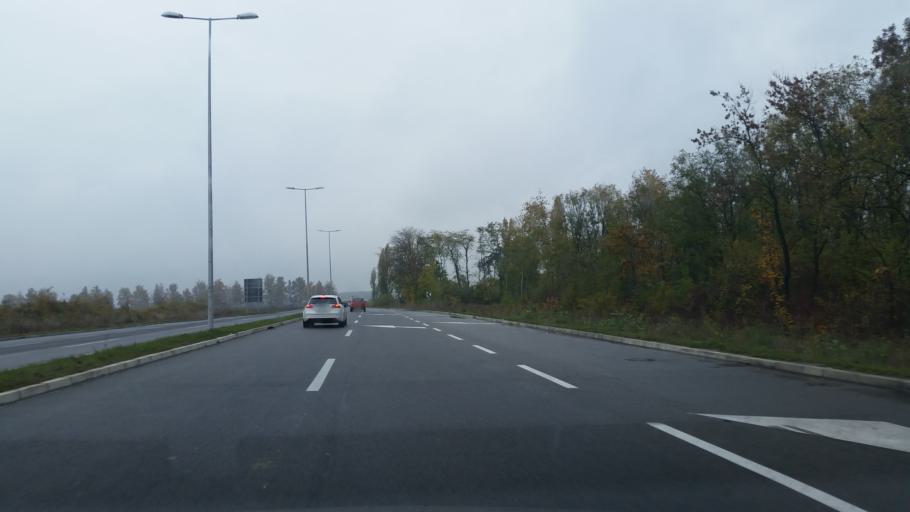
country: RS
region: Central Serbia
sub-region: Belgrade
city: Zemun
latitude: 44.9085
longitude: 20.4468
